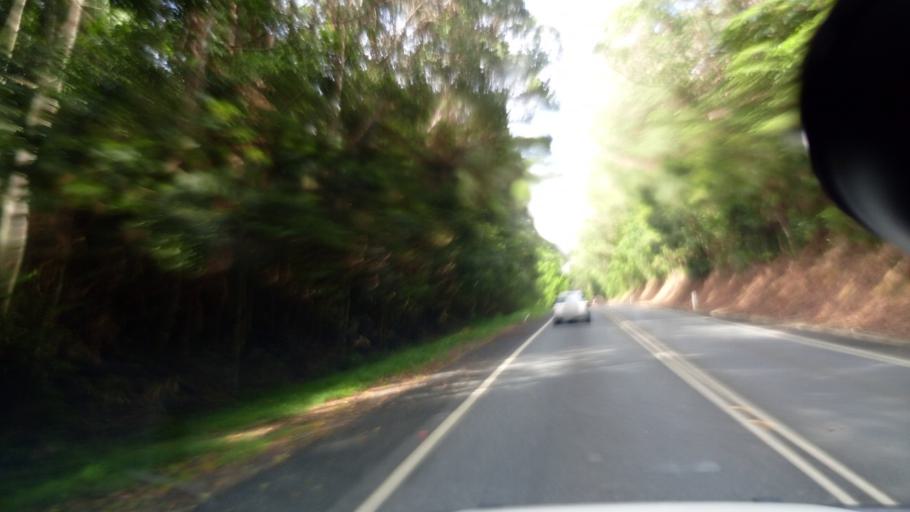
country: AU
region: Queensland
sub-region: Tablelands
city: Kuranda
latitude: -16.8201
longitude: 145.6301
